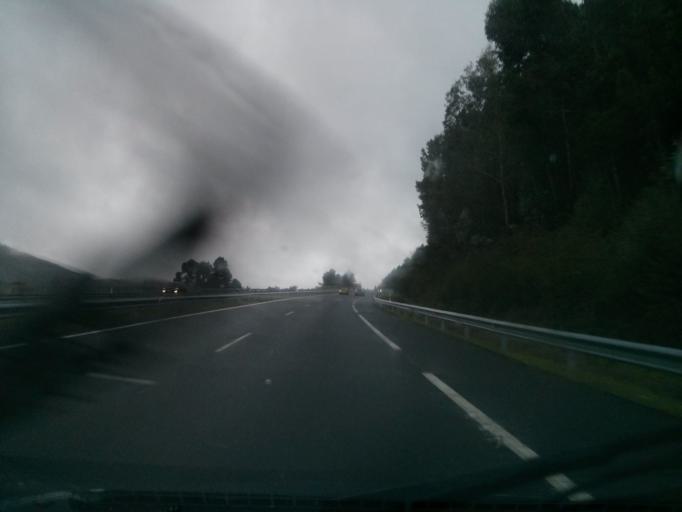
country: ES
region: Galicia
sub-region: Provincia de Ourense
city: Melon
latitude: 42.2537
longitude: -8.2235
